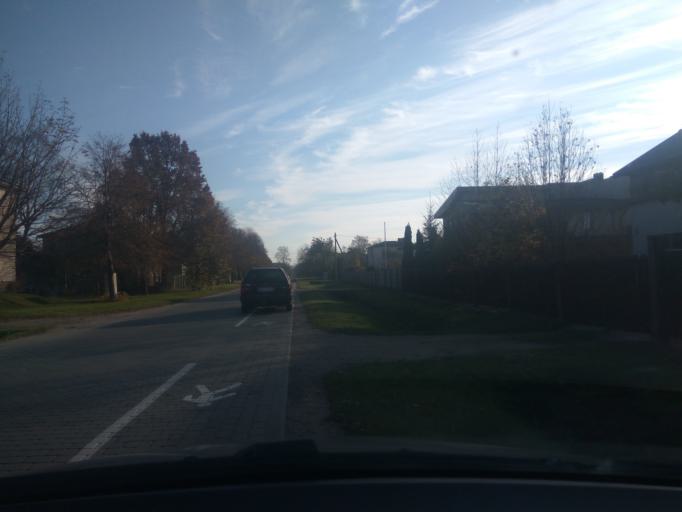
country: LV
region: Ventspils
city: Ventspils
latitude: 57.3815
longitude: 21.5774
